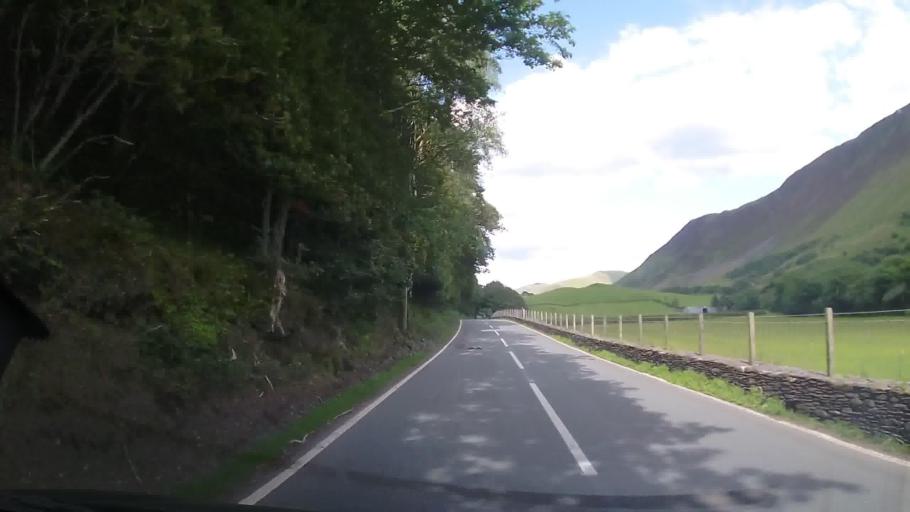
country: GB
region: Wales
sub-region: Gwynedd
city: Corris
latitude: 52.6607
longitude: -3.9250
